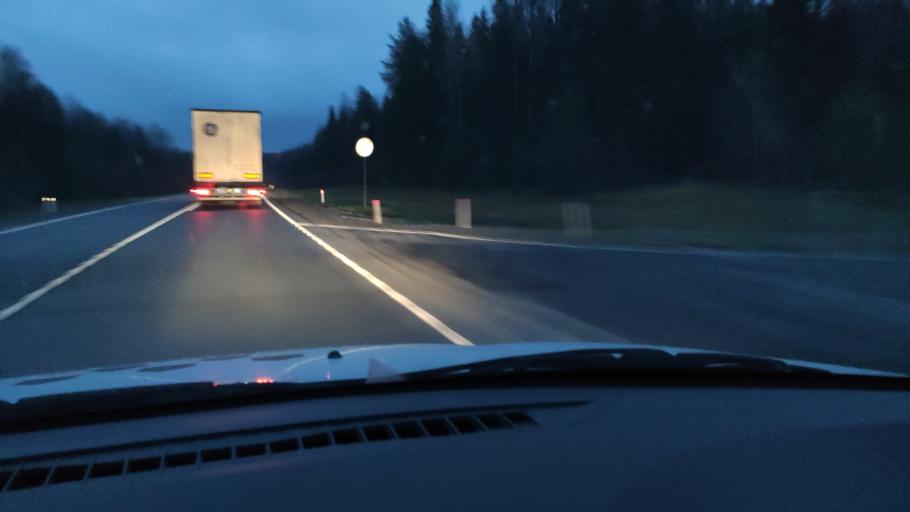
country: RU
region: Kirov
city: Kostino
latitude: 58.8282
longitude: 53.5348
